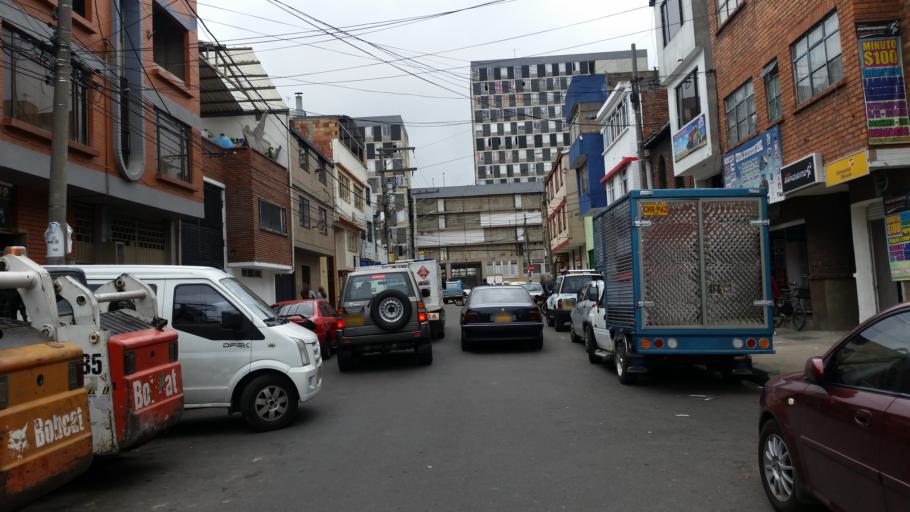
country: CO
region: Bogota D.C.
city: Bogota
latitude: 4.6214
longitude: -74.0893
